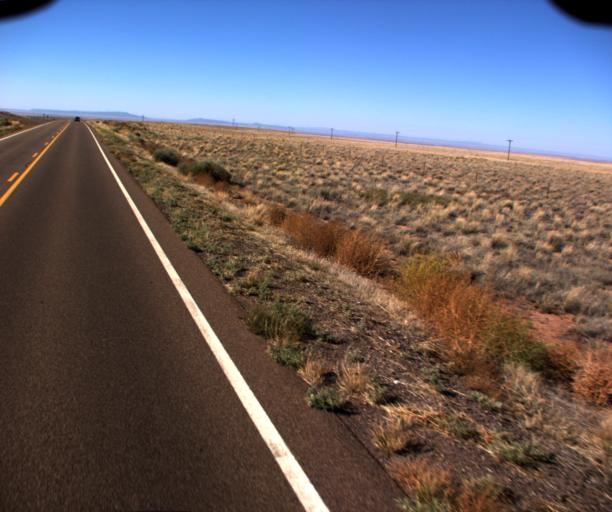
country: US
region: Arizona
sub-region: Navajo County
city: Winslow
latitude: 35.0848
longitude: -110.5542
